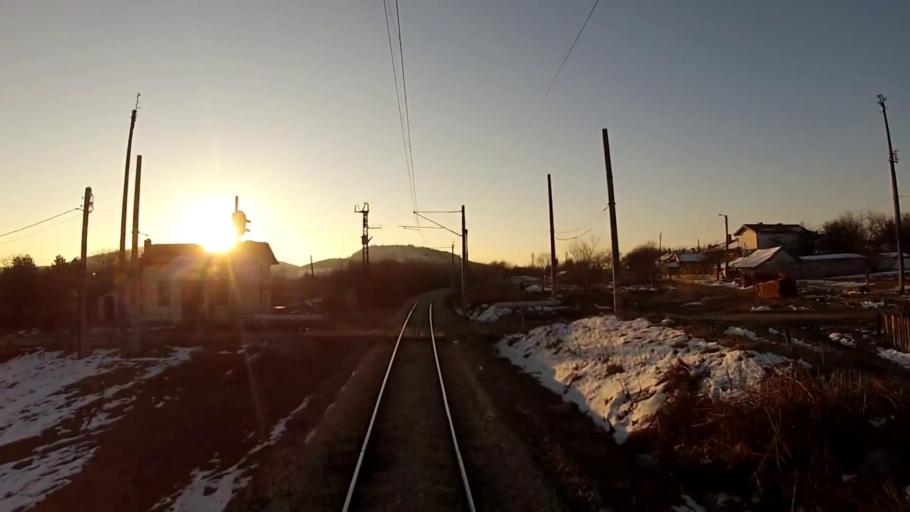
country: BG
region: Sofiya
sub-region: Obshtina Dragoman
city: Dragoman
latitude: 42.9083
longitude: 22.9445
